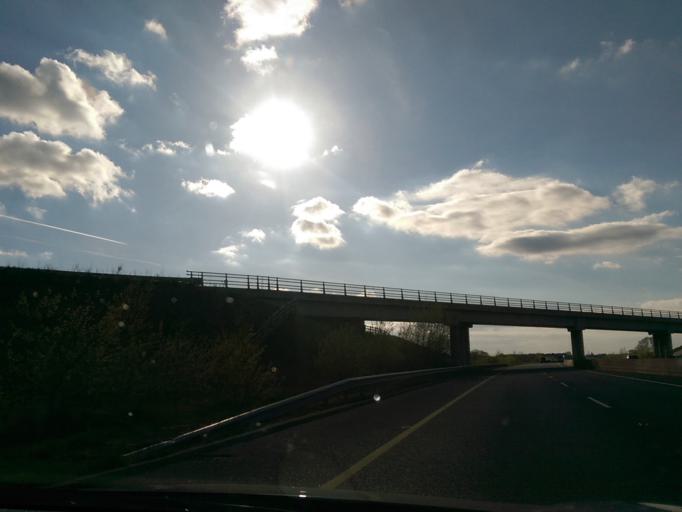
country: IE
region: Connaught
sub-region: County Galway
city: Athenry
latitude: 53.2758
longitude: -8.7168
